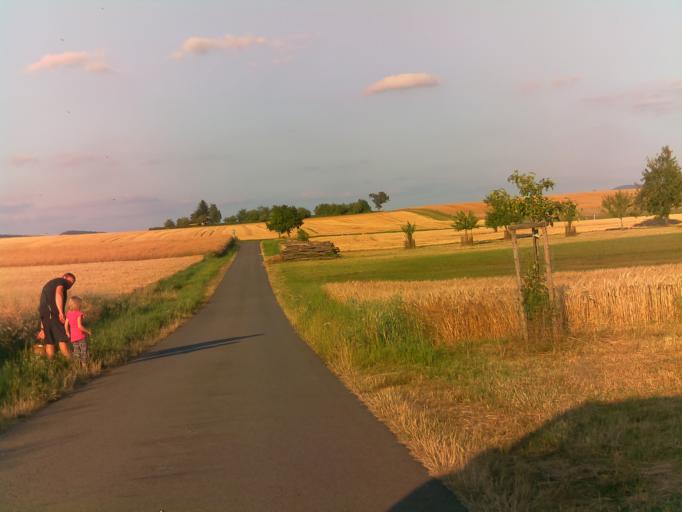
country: DE
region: Thuringia
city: Wolfershausen
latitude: 50.4420
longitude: 10.3966
